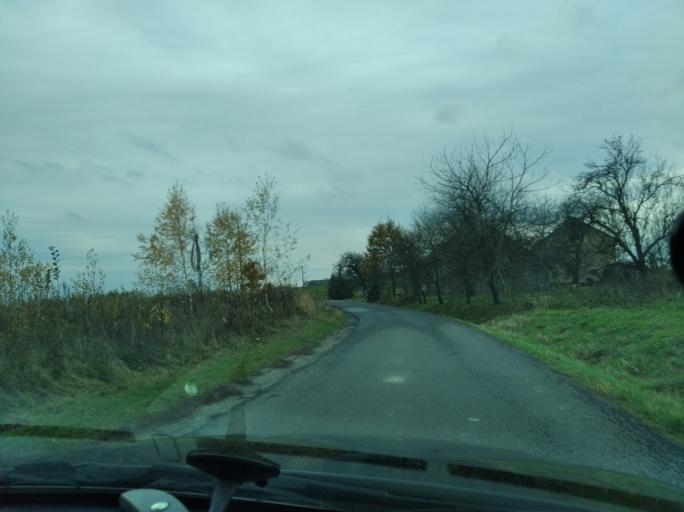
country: PL
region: Subcarpathian Voivodeship
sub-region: Powiat strzyzowski
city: Strzyzow
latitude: 49.9157
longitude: 21.7661
